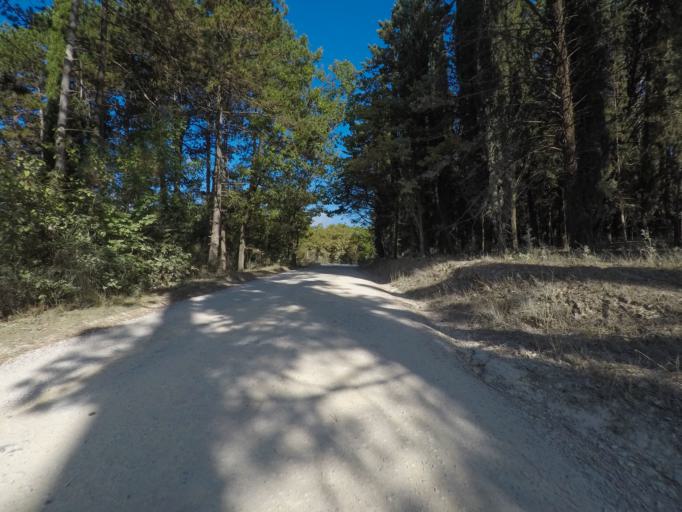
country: IT
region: Tuscany
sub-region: Provincia di Siena
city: Castellina in Chianti
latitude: 43.4359
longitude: 11.3114
